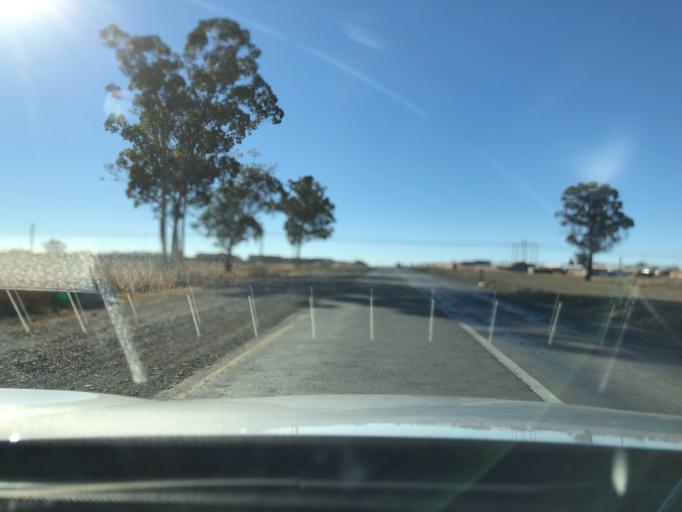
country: ZA
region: Mpumalanga
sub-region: Gert Sibande District Municipality
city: Standerton
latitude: -26.9393
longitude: 29.1994
